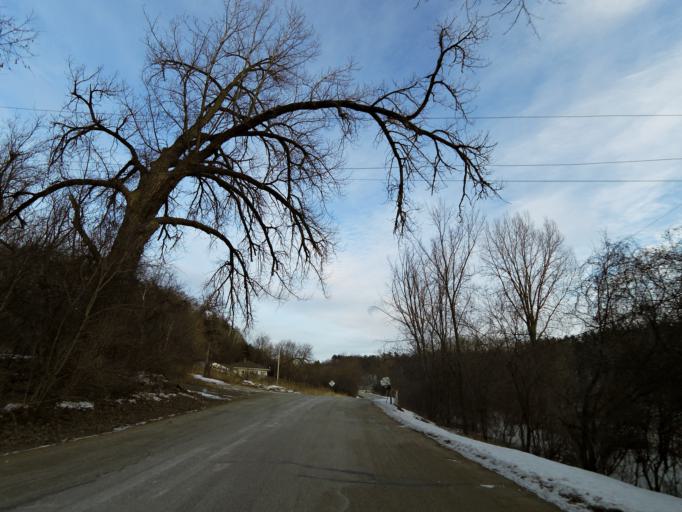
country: US
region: Minnesota
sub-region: Washington County
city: Afton
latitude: 44.9127
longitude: -92.8266
